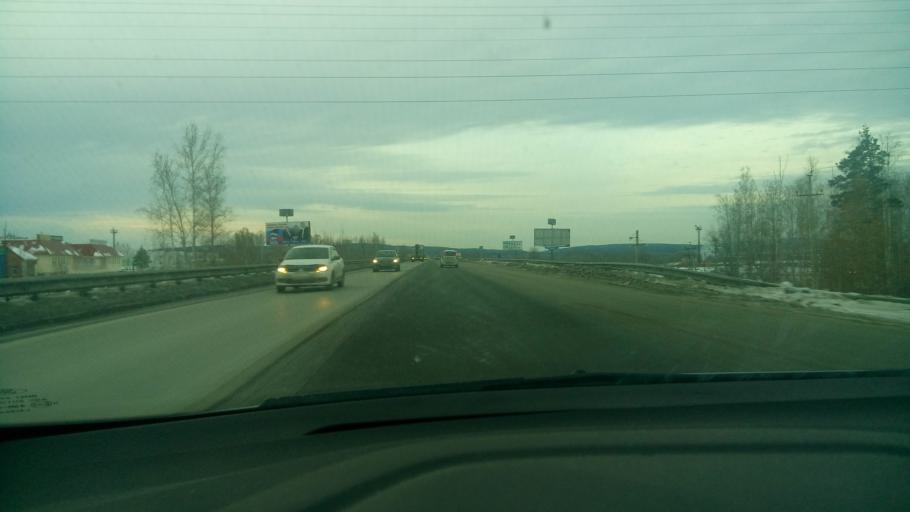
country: RU
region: Sverdlovsk
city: Istok
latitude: 56.7546
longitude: 60.7592
